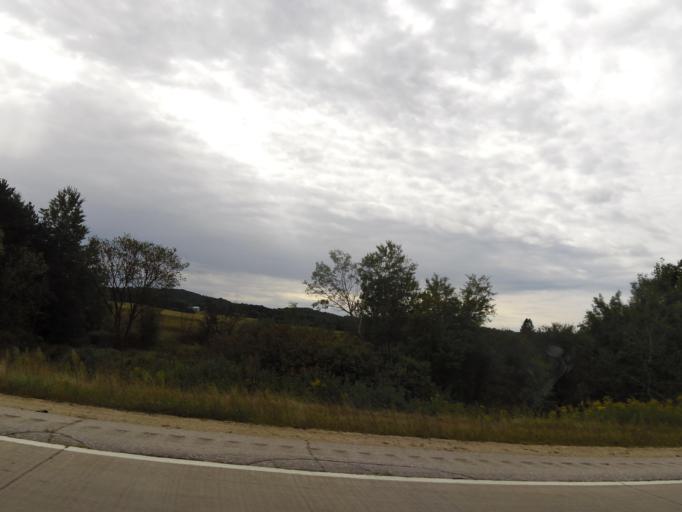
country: US
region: Wisconsin
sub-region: Monroe County
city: Sparta
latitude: 43.9214
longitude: -90.8148
